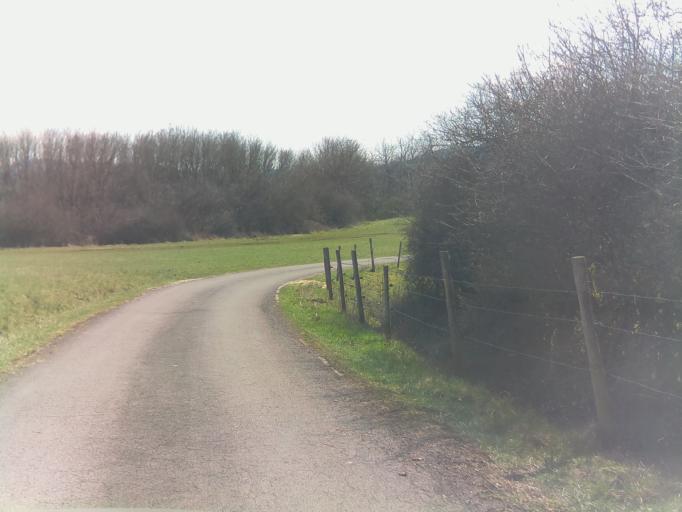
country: DE
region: Saarland
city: Nonnweiler
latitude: 49.5489
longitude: 6.9859
